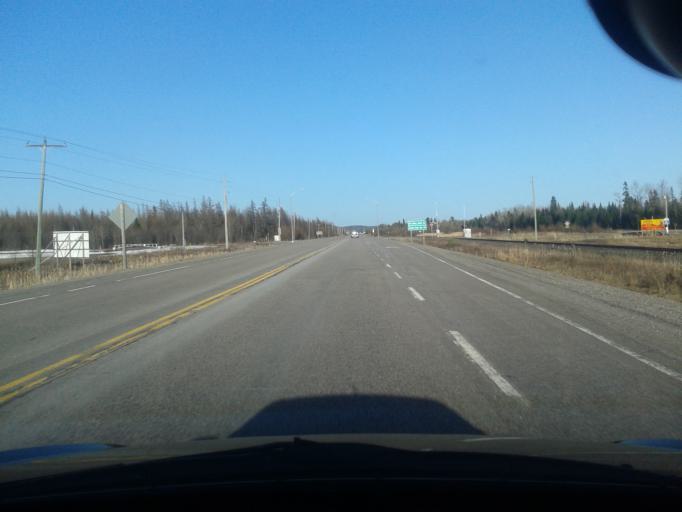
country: CA
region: Ontario
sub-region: Nipissing District
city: North Bay
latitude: 46.3689
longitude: -79.7597
